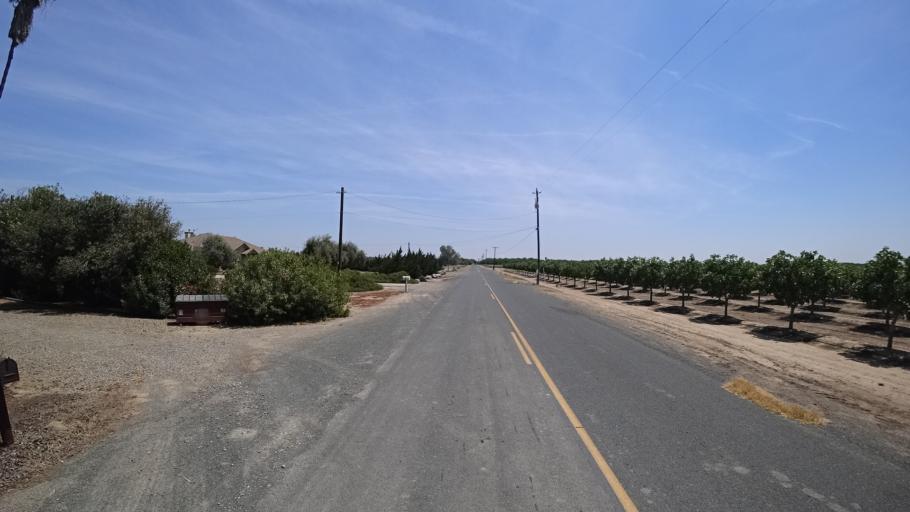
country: US
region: California
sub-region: Fresno County
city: Riverdale
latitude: 36.3948
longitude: -119.8173
